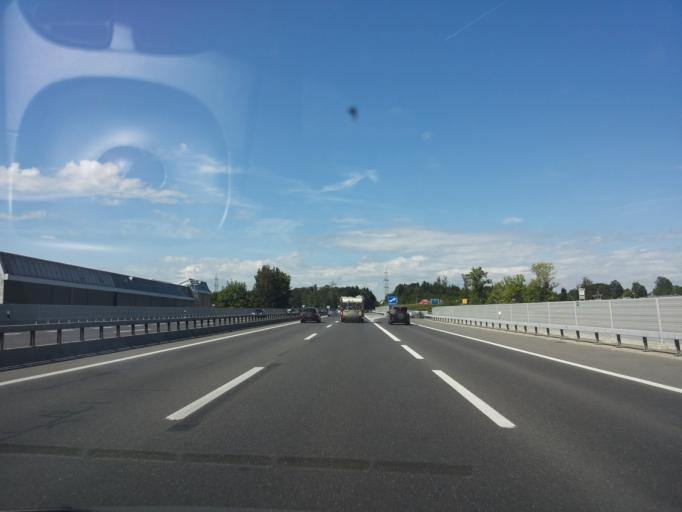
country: CH
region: Lucerne
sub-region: Hochdorf District
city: Emmen
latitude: 47.0879
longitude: 8.2533
